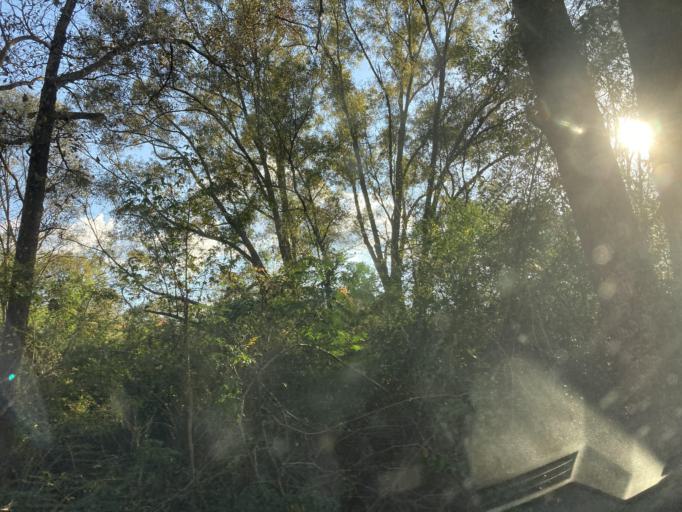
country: US
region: Mississippi
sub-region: Lamar County
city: Sumrall
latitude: 31.4071
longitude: -89.6519
